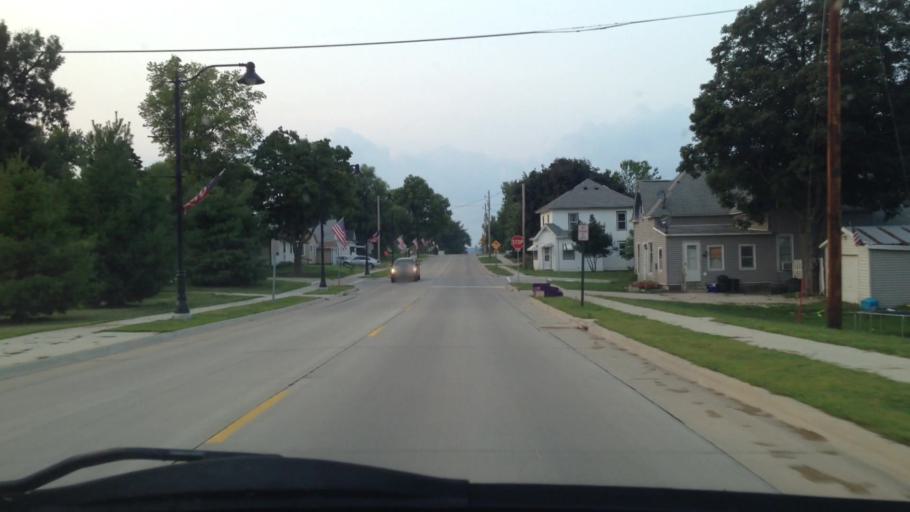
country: US
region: Iowa
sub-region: Benton County
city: Urbana
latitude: 42.2243
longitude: -91.8714
